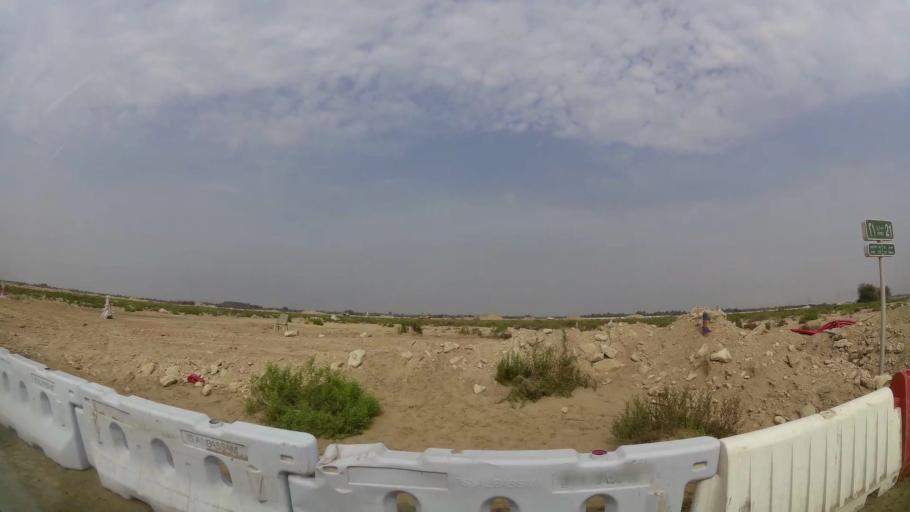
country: AE
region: Abu Dhabi
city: Abu Dhabi
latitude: 24.6548
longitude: 54.7400
